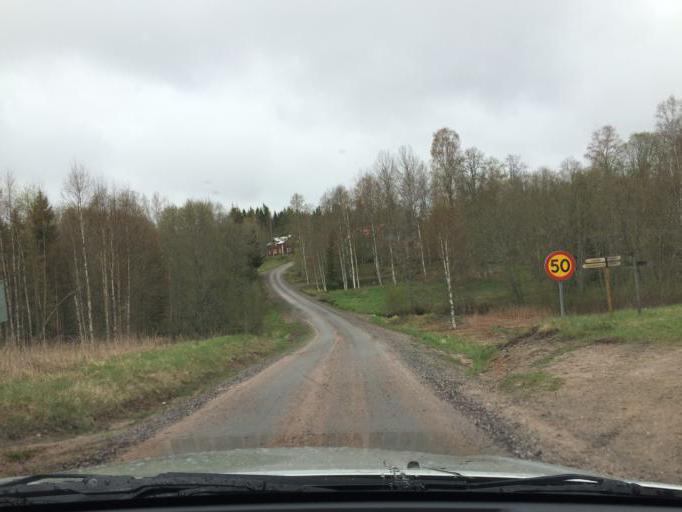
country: SE
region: Dalarna
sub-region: Ludvika Kommun
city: Abborrberget
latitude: 60.0205
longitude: 14.6220
